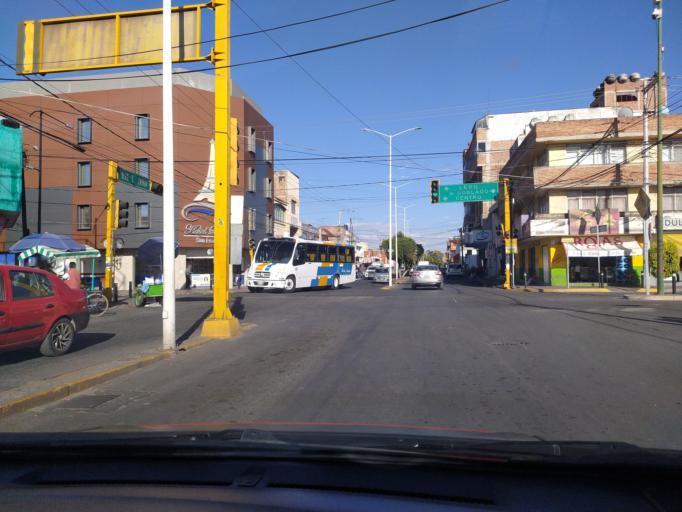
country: LA
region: Oudomxai
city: Muang La
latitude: 21.0155
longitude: 101.8580
